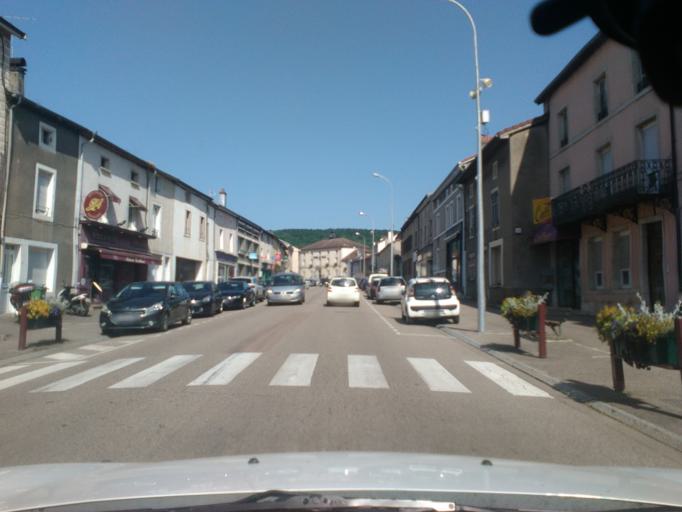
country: FR
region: Lorraine
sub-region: Departement des Vosges
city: Chatenois
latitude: 48.3020
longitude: 5.8357
